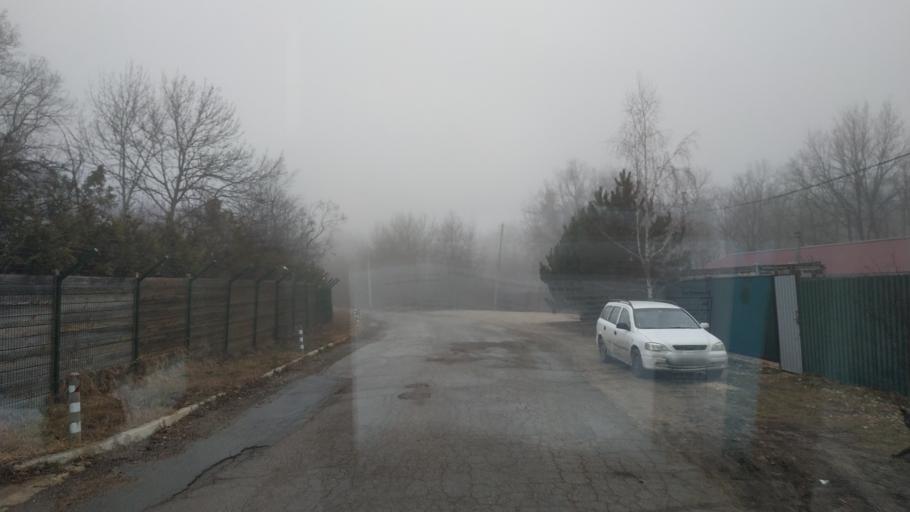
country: MD
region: Laloveni
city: Ialoveni
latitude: 46.9475
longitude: 28.6998
